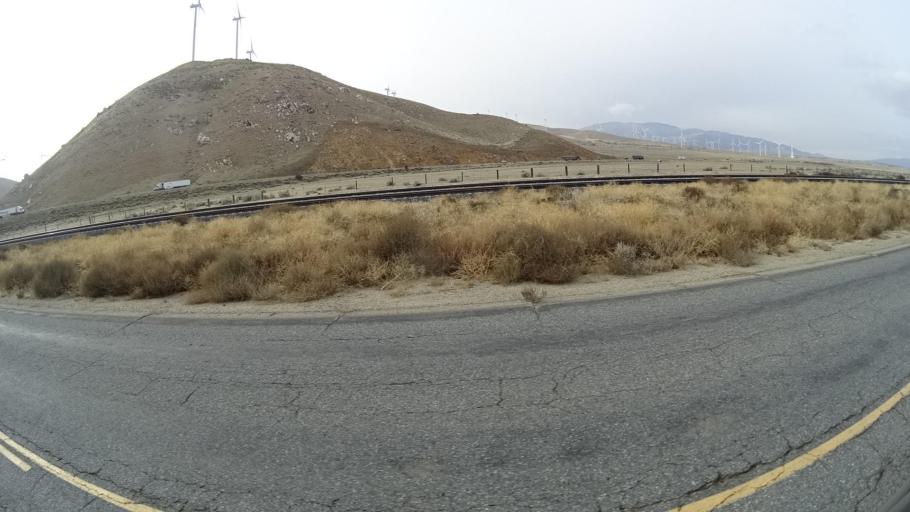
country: US
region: California
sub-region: Kern County
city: Tehachapi
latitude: 35.1128
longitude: -118.3294
